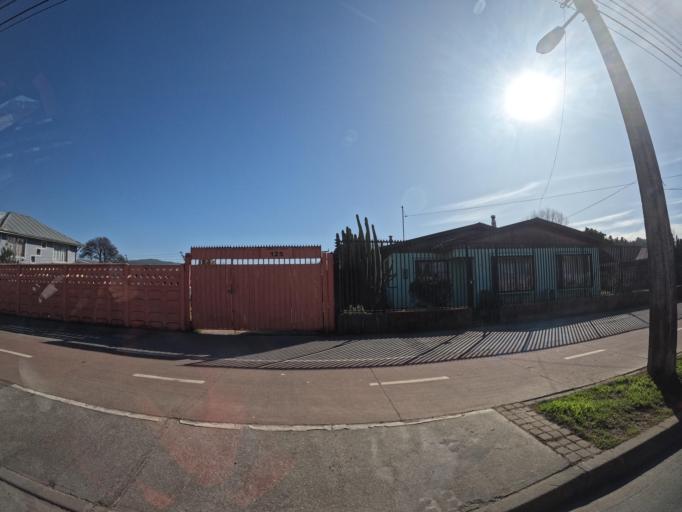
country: CL
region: Biobio
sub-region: Provincia de Concepcion
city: Chiguayante
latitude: -36.9705
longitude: -72.9364
